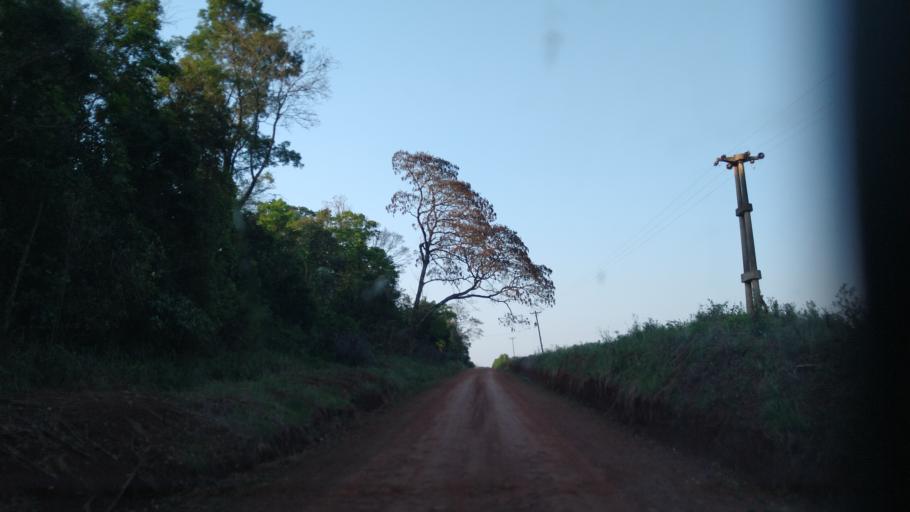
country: AR
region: Misiones
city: Jardin America
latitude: -27.0821
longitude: -55.2743
